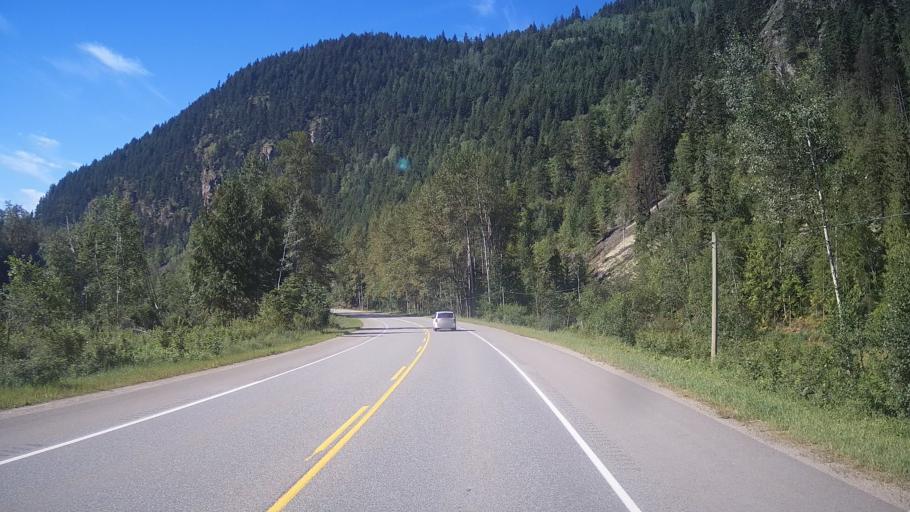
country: CA
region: British Columbia
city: Kamloops
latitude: 51.4839
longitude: -120.1826
